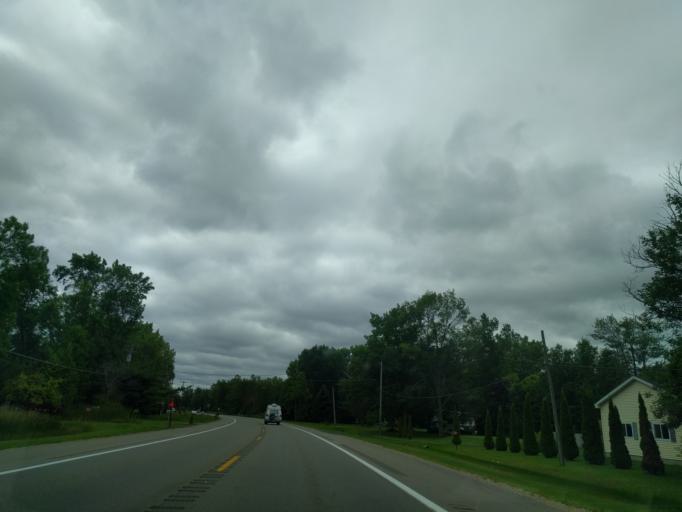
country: US
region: Michigan
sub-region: Menominee County
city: Menominee
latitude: 45.1638
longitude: -87.5891
